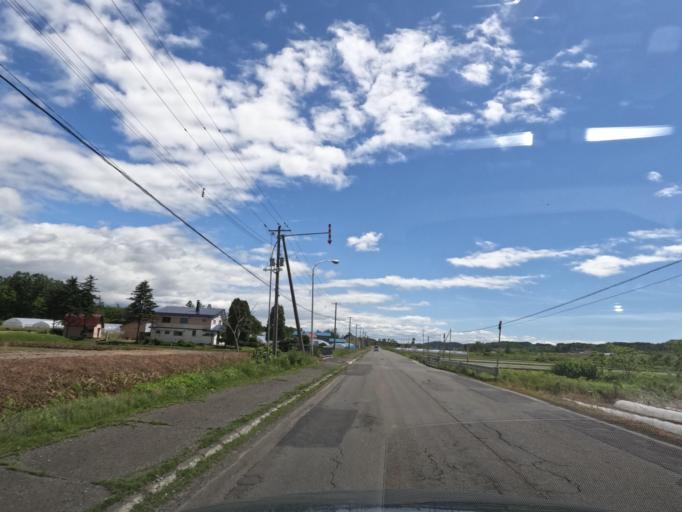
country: JP
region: Hokkaido
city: Iwamizawa
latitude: 43.1410
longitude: 141.8055
